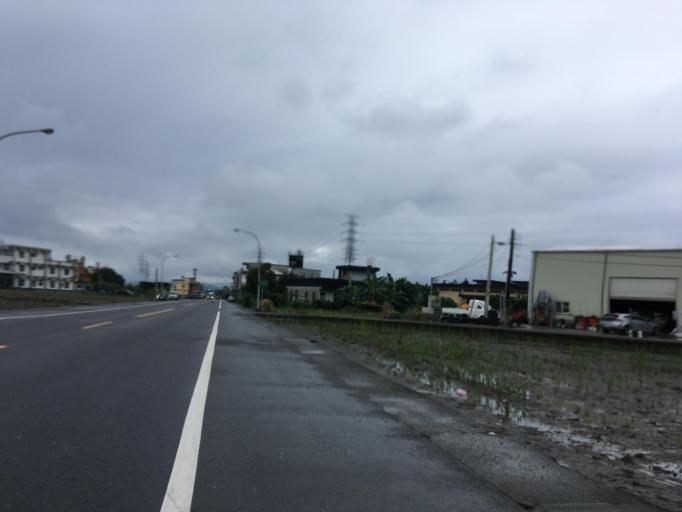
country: TW
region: Taiwan
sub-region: Yilan
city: Yilan
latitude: 24.6627
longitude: 121.7520
